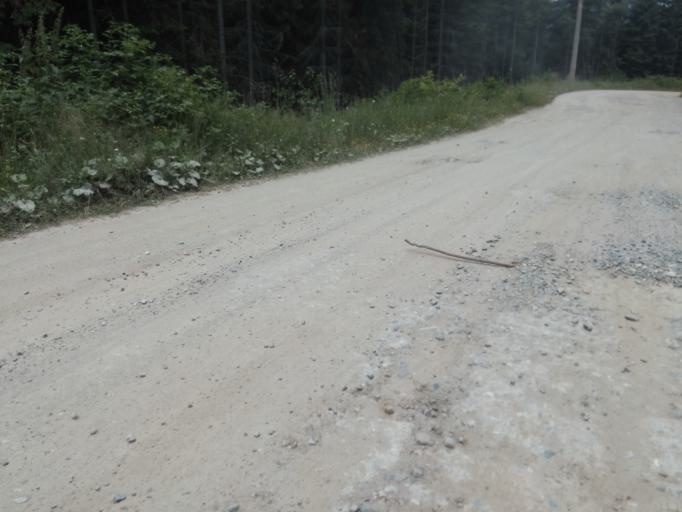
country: RO
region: Valcea
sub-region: Comuna Voineasa
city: Voineasa
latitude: 45.4344
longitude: 23.7617
